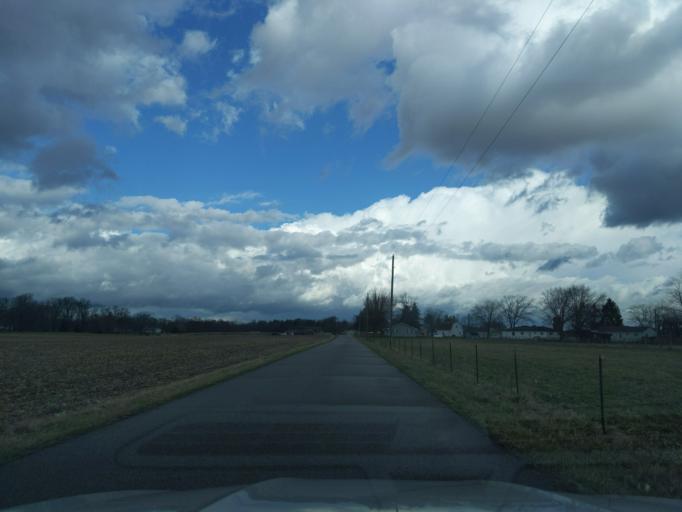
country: US
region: Indiana
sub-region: Decatur County
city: Saint Paul
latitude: 39.3988
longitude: -85.5598
